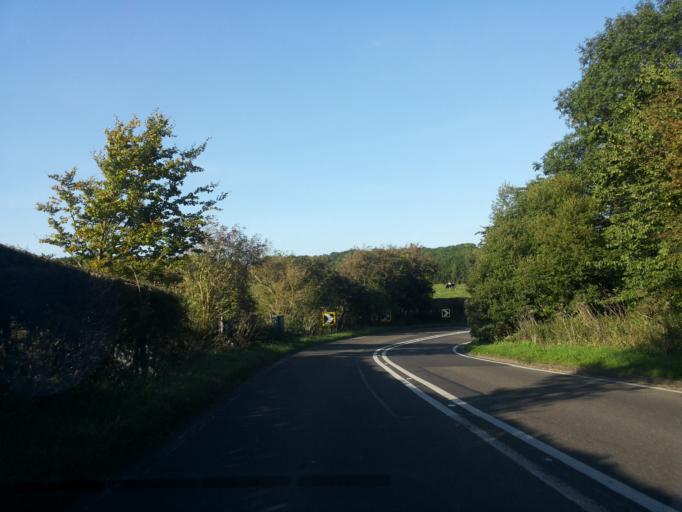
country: GB
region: England
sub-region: Derbyshire
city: Bakewell
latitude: 53.2369
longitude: -1.6541
